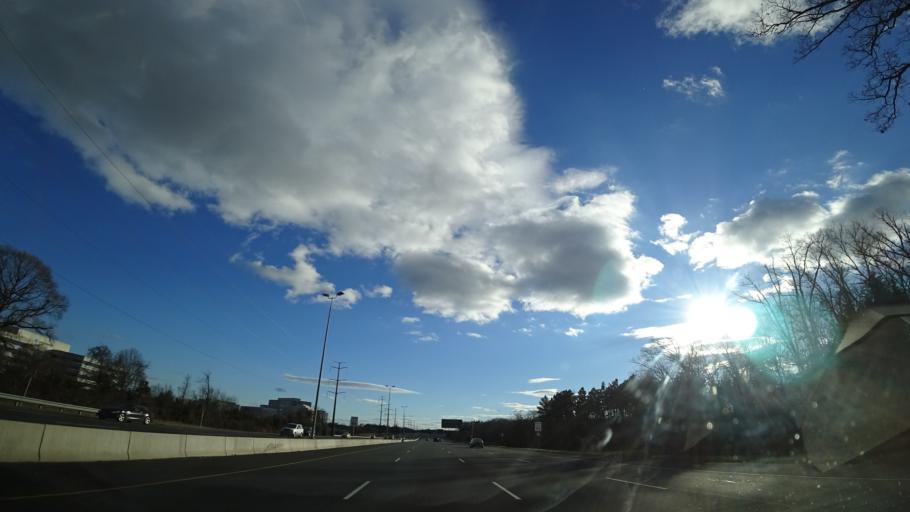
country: US
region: Virginia
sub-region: Fairfax County
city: Floris
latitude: 38.9240
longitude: -77.4302
